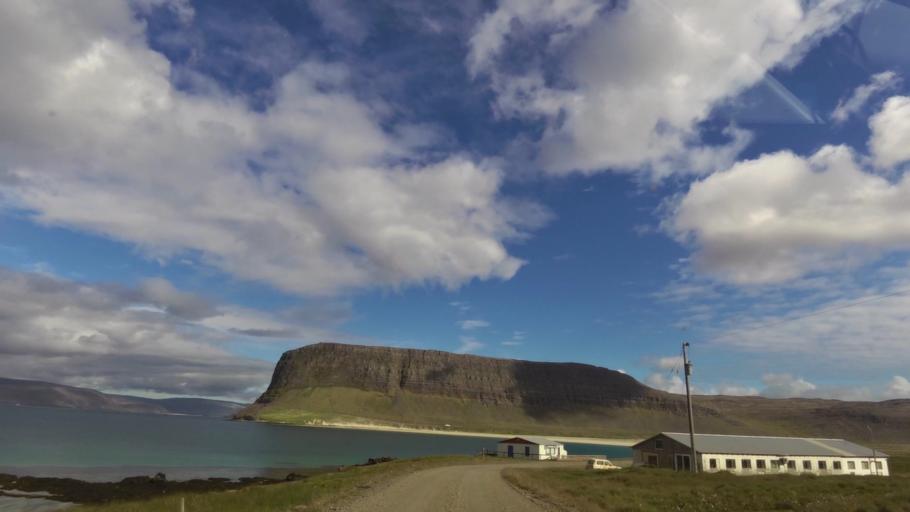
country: IS
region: West
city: Olafsvik
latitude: 65.5917
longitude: -24.1246
